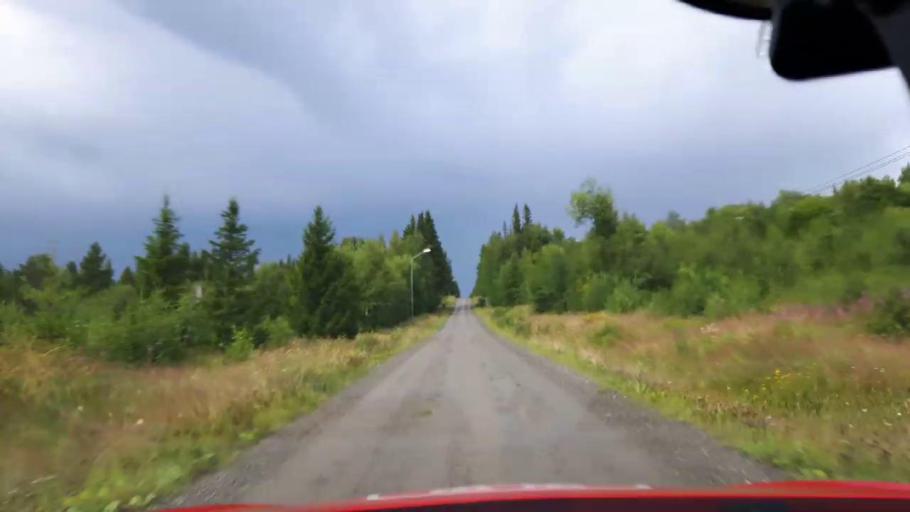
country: SE
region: Jaemtland
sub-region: Stroemsunds Kommun
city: Stroemsund
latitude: 64.0611
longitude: 15.8898
